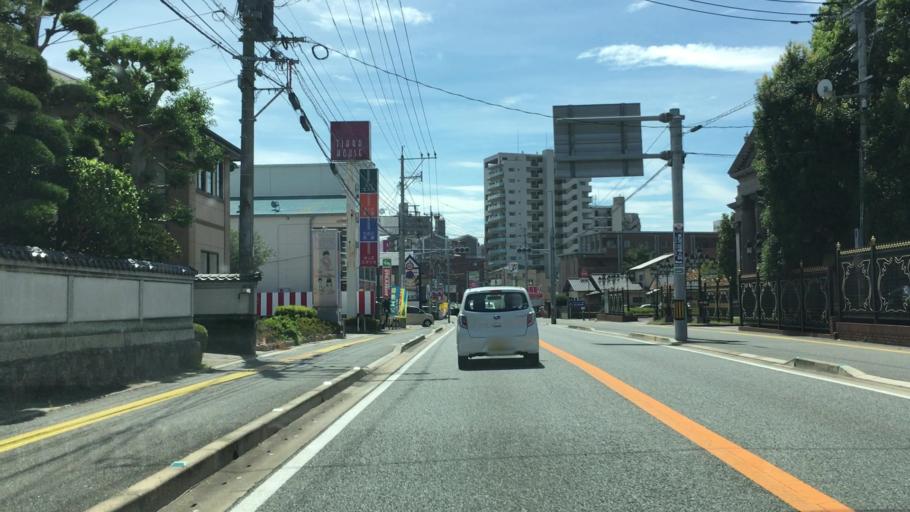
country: JP
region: Fukuoka
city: Onojo
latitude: 33.5422
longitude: 130.4728
